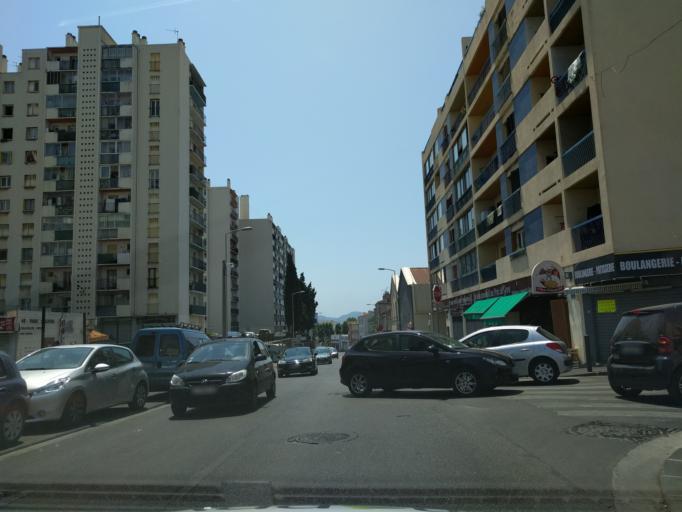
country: FR
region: Provence-Alpes-Cote d'Azur
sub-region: Departement des Bouches-du-Rhone
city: Marseille 14
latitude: 43.3442
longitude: 5.3595
